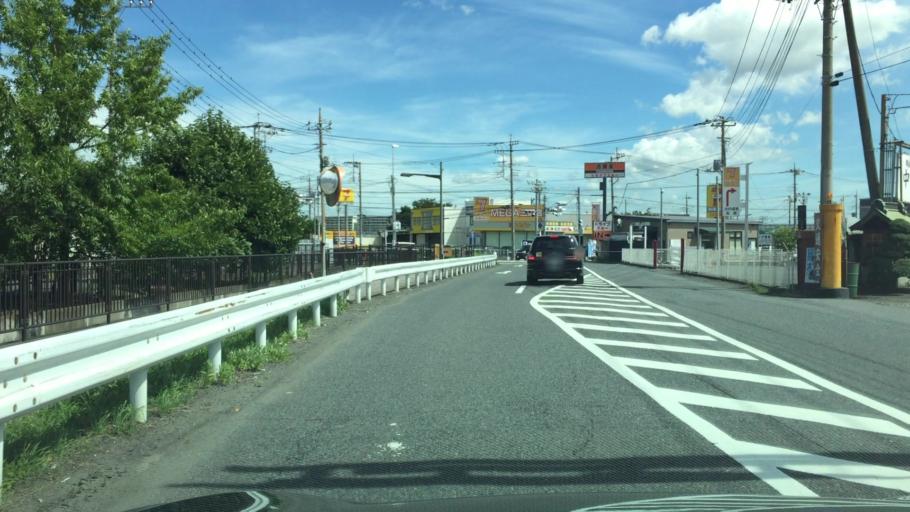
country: JP
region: Saitama
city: Yashio-shi
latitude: 35.8488
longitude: 139.8536
